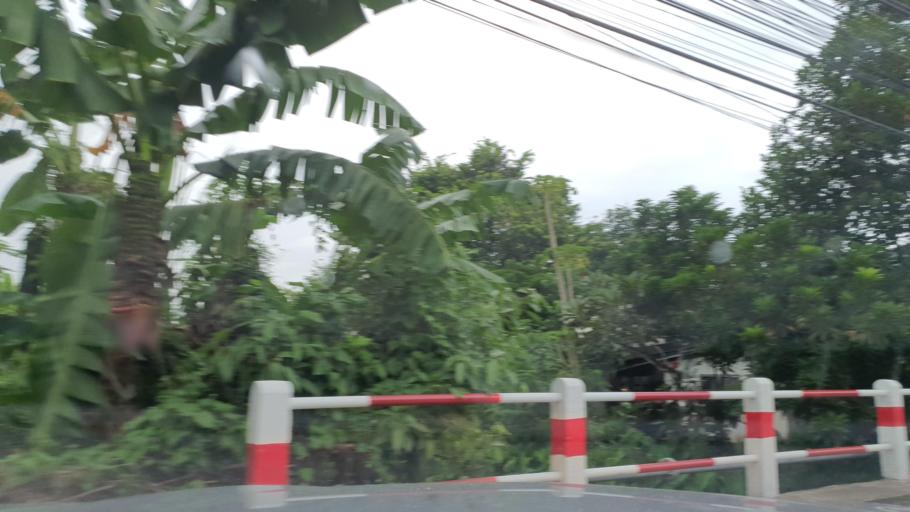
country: TH
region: Chiang Mai
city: San Sai
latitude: 18.9167
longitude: 98.9496
